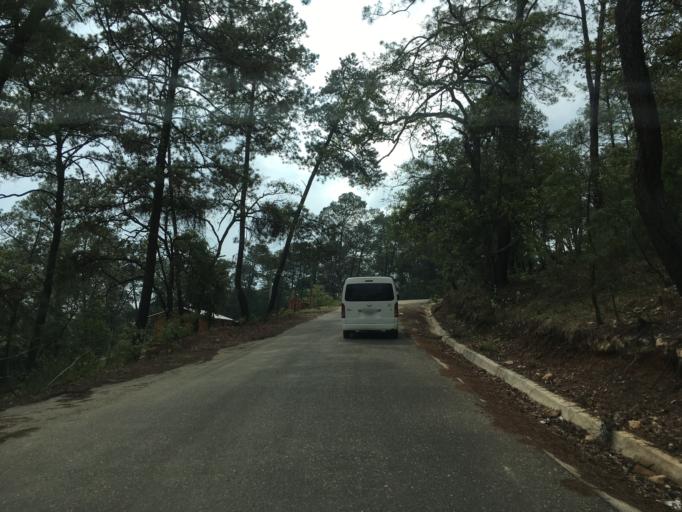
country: MX
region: Oaxaca
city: Santiago Tilantongo
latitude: 17.2106
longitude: -97.2794
